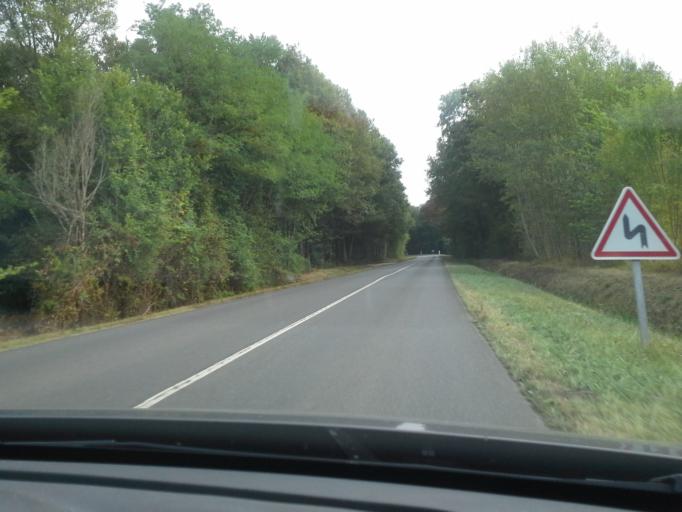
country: FR
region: Centre
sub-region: Departement du Loir-et-Cher
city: Herbault
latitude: 47.5865
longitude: 1.2021
